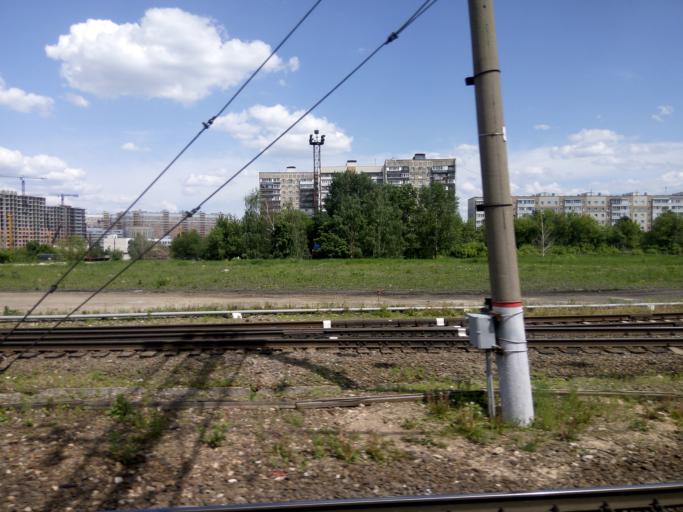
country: RU
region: Moskovskaya
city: Biryulevo Zapadnoye
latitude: 55.6001
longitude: 37.6497
